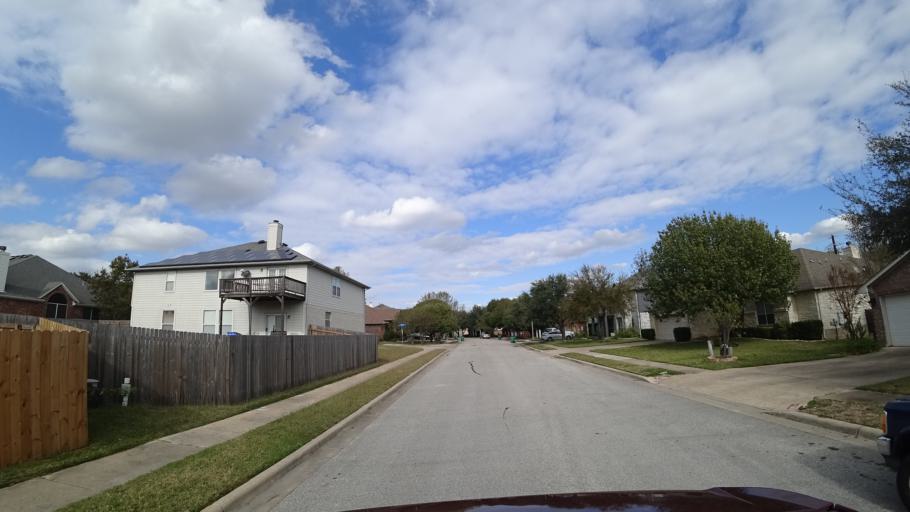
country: US
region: Texas
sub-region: Travis County
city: Pflugerville
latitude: 30.4268
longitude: -97.6274
